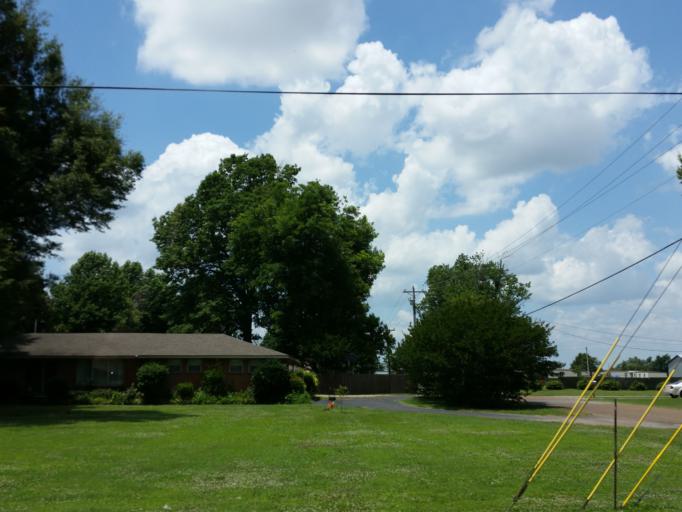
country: US
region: Tennessee
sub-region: Lake County
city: Ridgely
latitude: 36.2713
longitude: -89.4780
